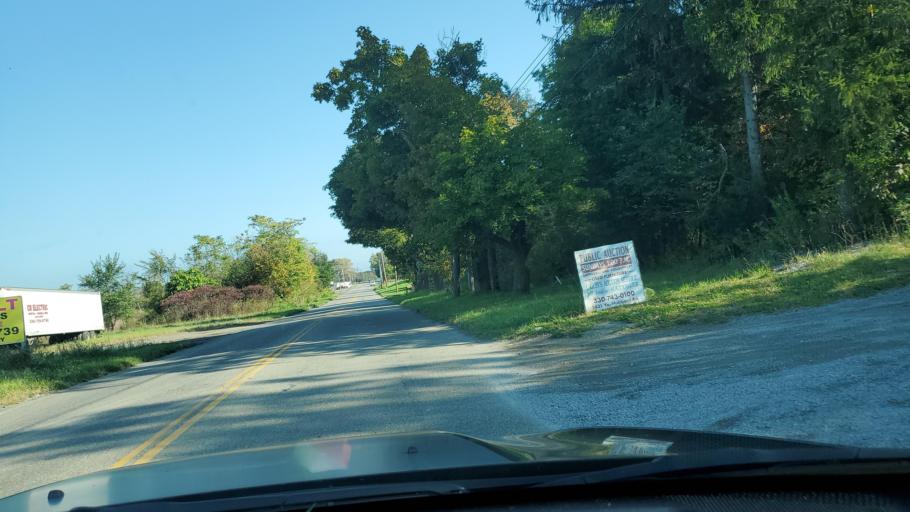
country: US
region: Ohio
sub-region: Mahoning County
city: Youngstown
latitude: 41.1316
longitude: -80.6252
